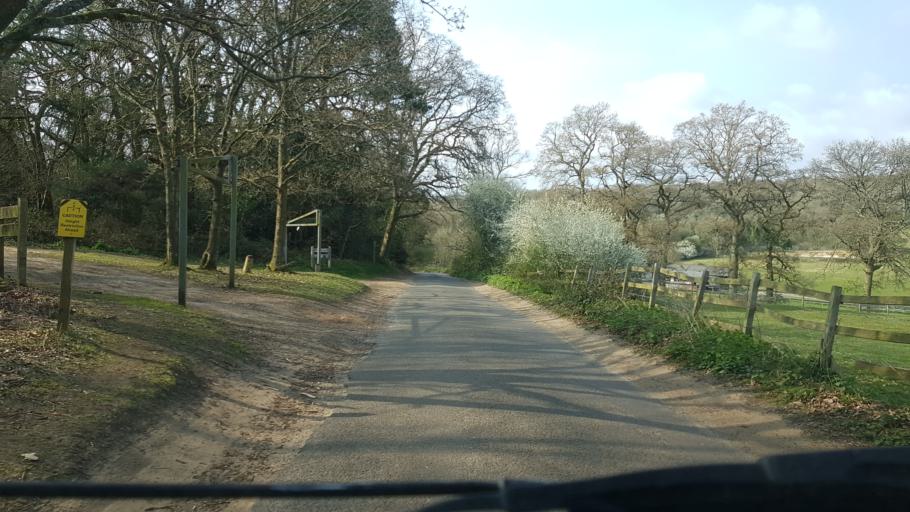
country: GB
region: England
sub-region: Surrey
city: Chilworth
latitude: 51.2264
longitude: -0.5182
